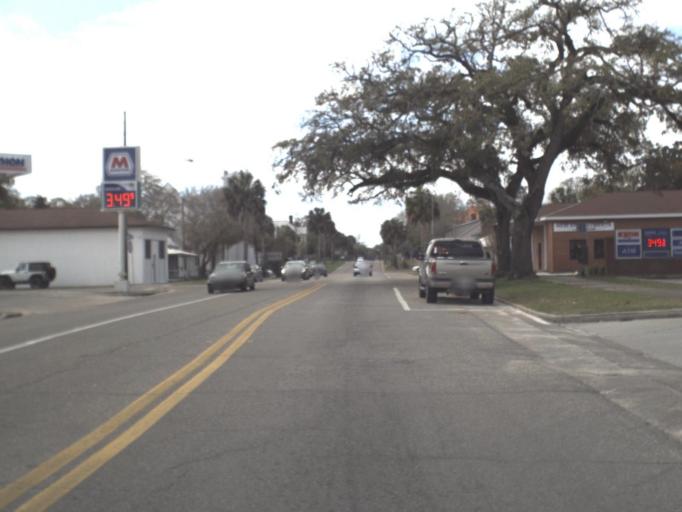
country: US
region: Florida
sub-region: Franklin County
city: Apalachicola
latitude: 29.7276
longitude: -84.9850
